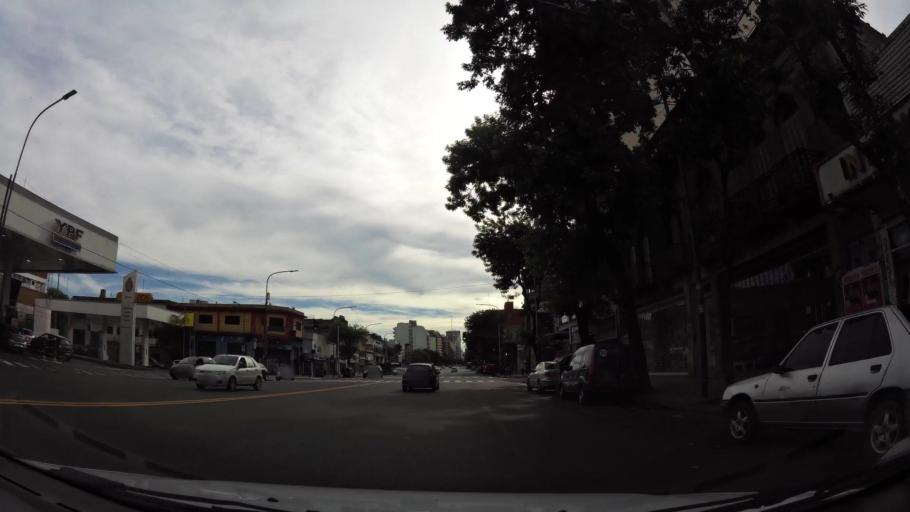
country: AR
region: Buenos Aires F.D.
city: Villa Santa Rita
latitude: -34.6311
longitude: -58.4719
